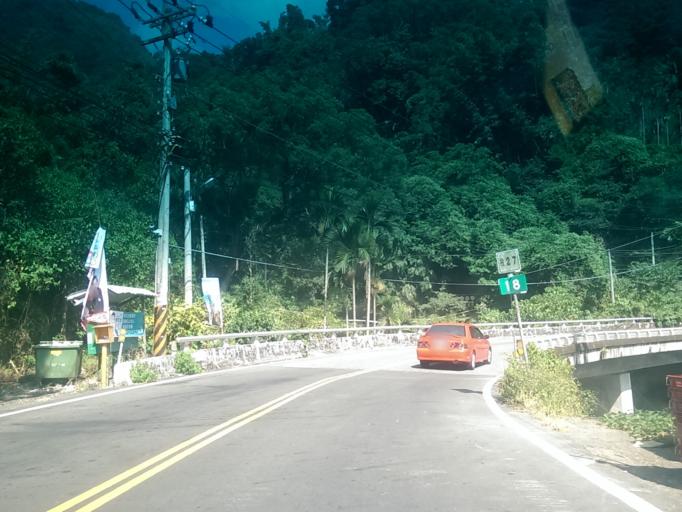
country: TW
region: Taiwan
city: Lugu
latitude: 23.8274
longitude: 120.8372
